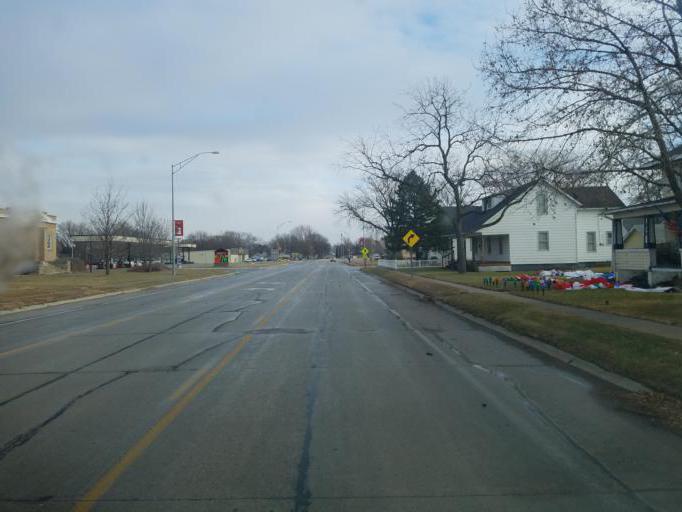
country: US
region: Nebraska
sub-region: Pierce County
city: Pierce
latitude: 42.1963
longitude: -97.5258
